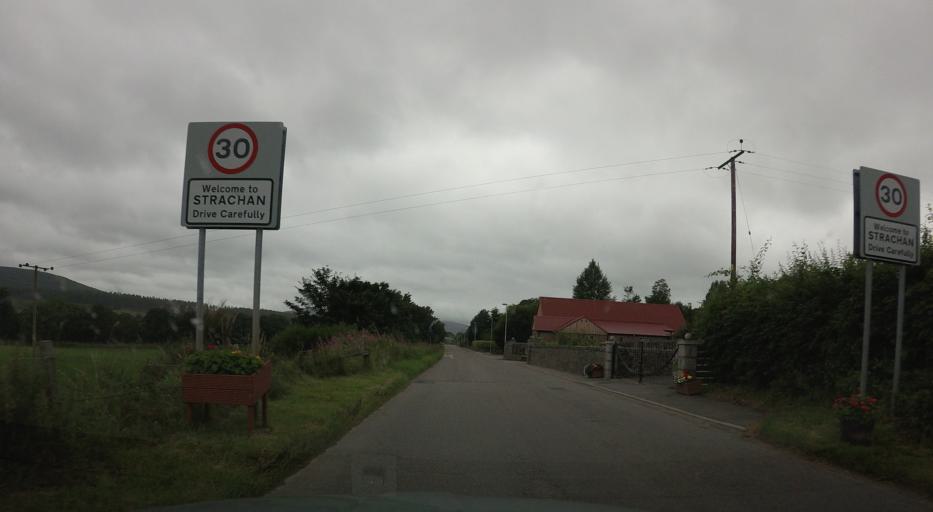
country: GB
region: Scotland
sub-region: Aberdeenshire
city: Banchory
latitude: 57.0225
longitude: -2.5291
